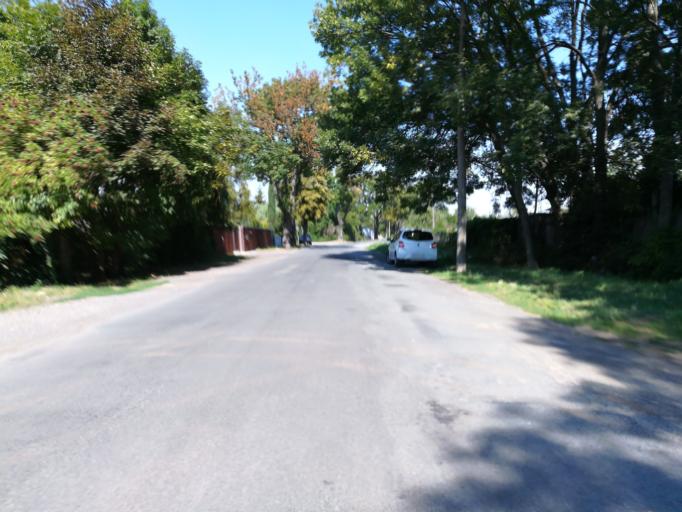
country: DE
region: Saxony-Anhalt
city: Neue Neustadt
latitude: 52.1446
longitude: 11.6109
